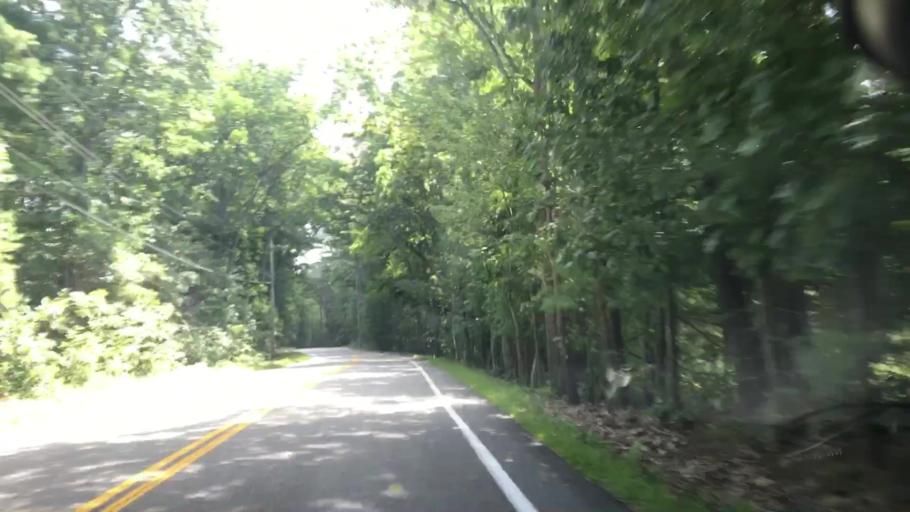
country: US
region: New Hampshire
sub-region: Hillsborough County
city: Bedford
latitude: 42.9180
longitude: -71.5686
